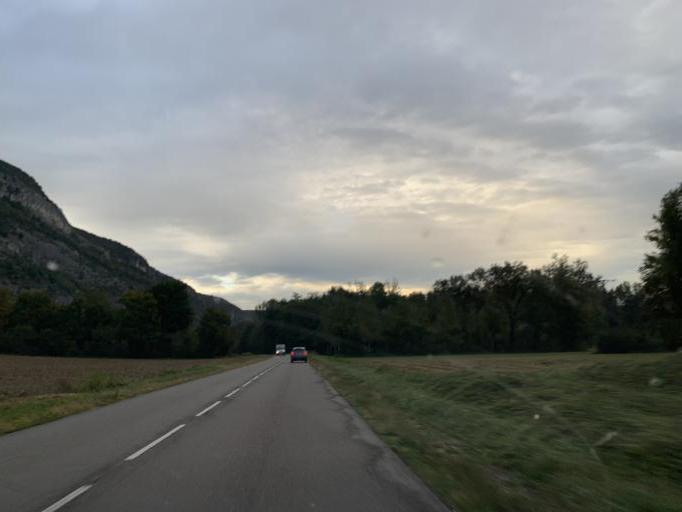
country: FR
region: Rhone-Alpes
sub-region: Departement de l'Isere
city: Les Avenieres
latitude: 45.6860
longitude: 5.5947
